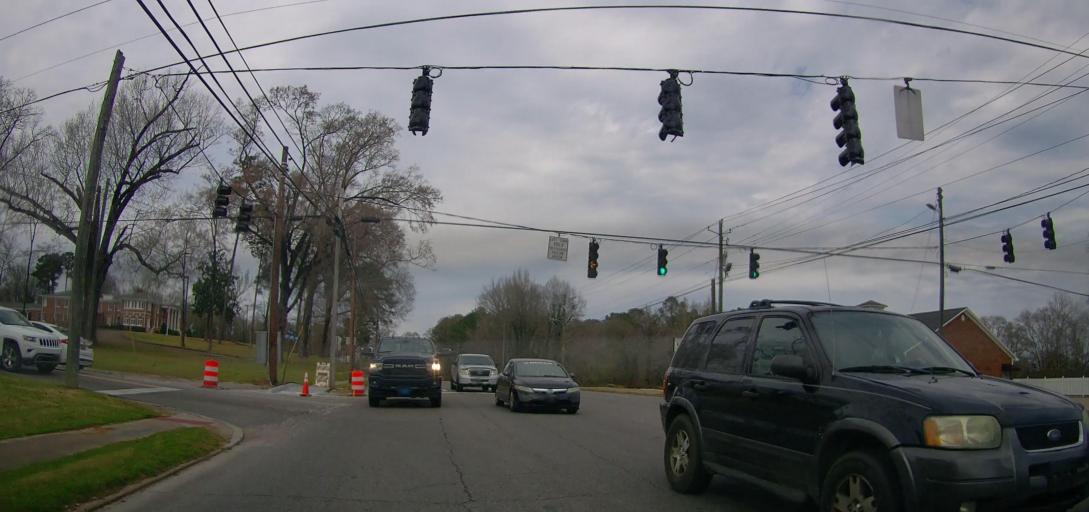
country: US
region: Alabama
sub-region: Marion County
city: Hamilton
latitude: 34.1322
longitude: -87.9901
